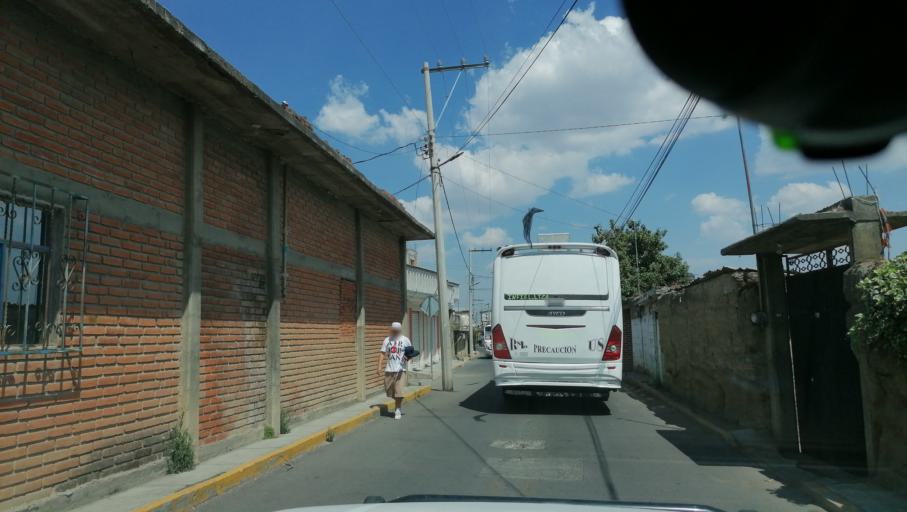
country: MX
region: Puebla
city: San Andres Calpan
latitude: 19.1037
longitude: -98.4824
